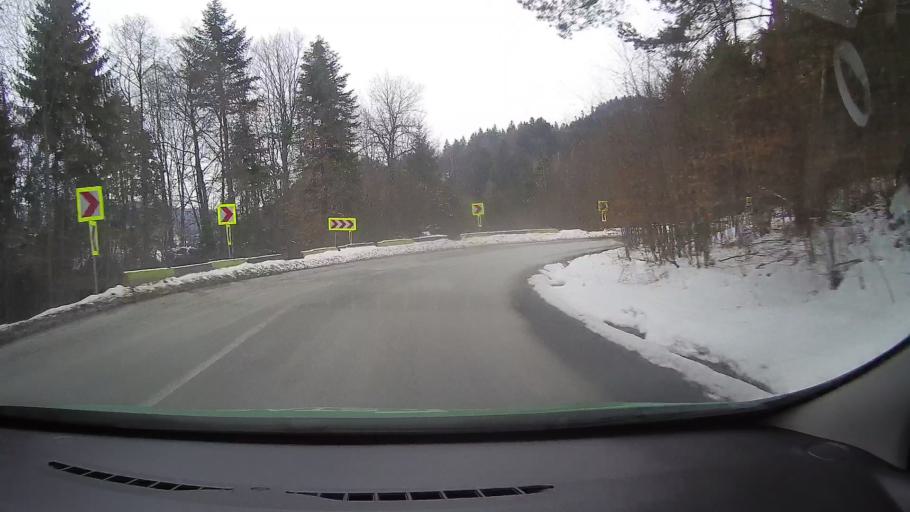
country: RO
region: Brasov
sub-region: Oras Predeal
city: Predeal
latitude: 45.5181
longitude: 25.5056
